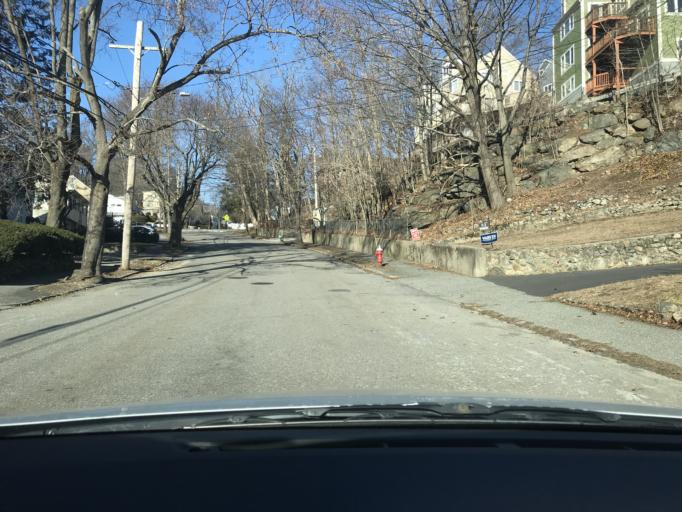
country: US
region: Massachusetts
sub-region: Middlesex County
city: Arlington
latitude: 42.4262
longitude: -71.1553
